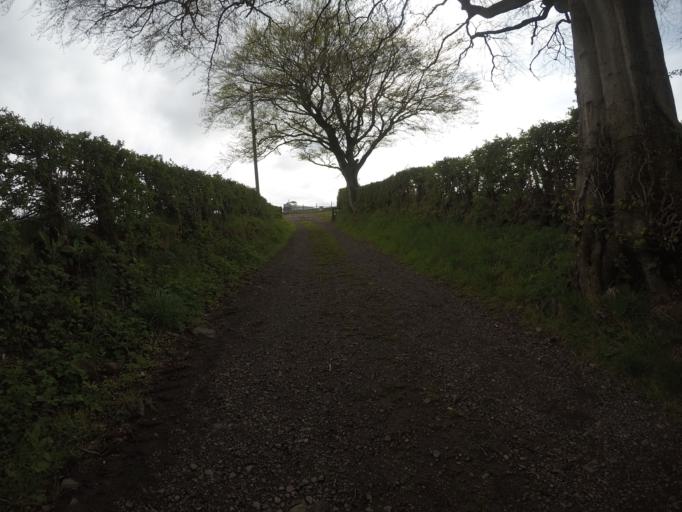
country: GB
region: Scotland
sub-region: East Renfrewshire
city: Newton Mearns
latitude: 55.7593
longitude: -4.3172
